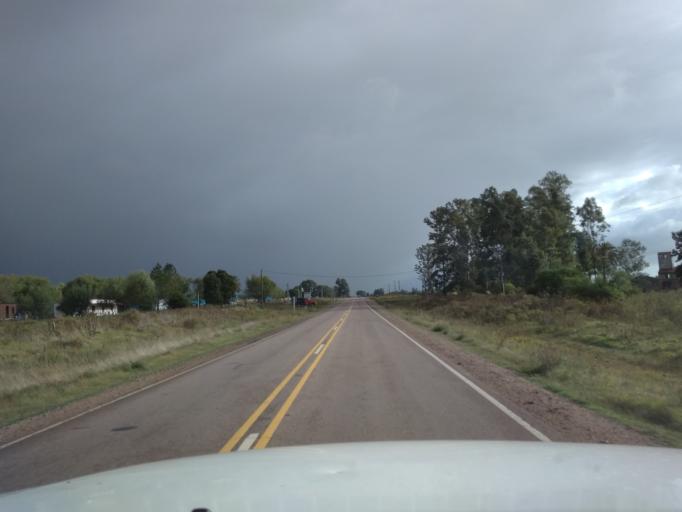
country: UY
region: Canelones
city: Tala
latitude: -34.3705
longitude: -55.7843
